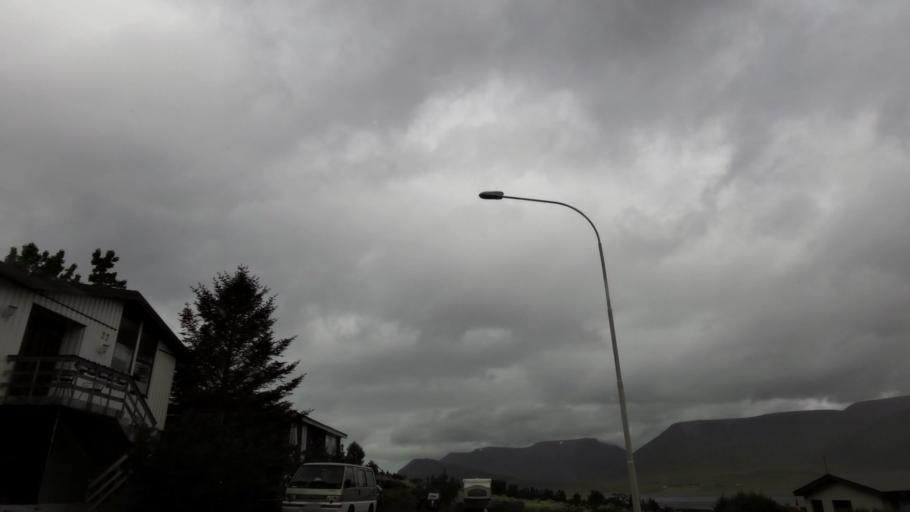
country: IS
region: Westfjords
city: Isafjoerdur
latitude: 65.8753
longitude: -23.4916
